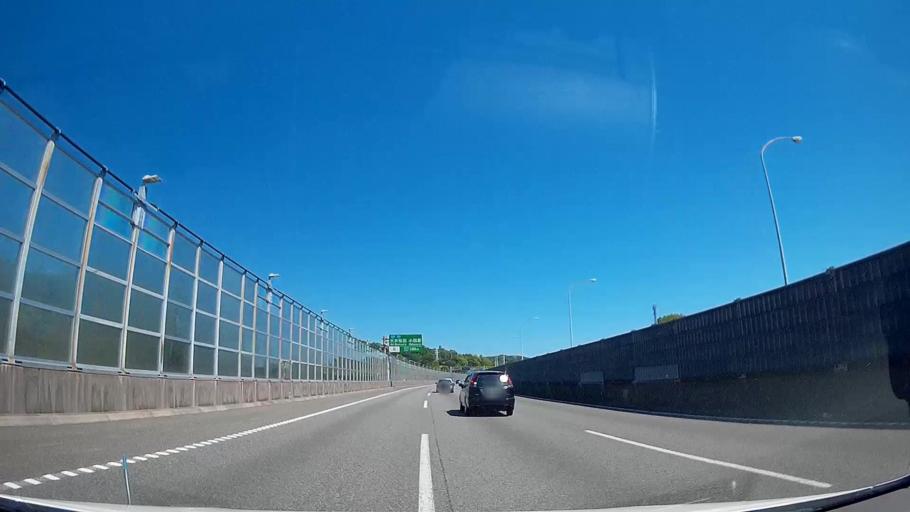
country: JP
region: Kanagawa
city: Hadano
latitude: 35.3485
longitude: 139.1504
